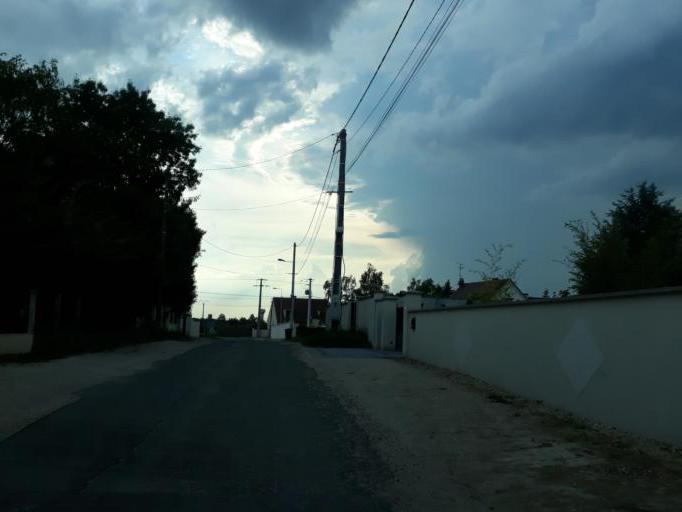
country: FR
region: Centre
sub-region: Departement du Loiret
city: Chaingy
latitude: 47.8855
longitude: 1.7904
